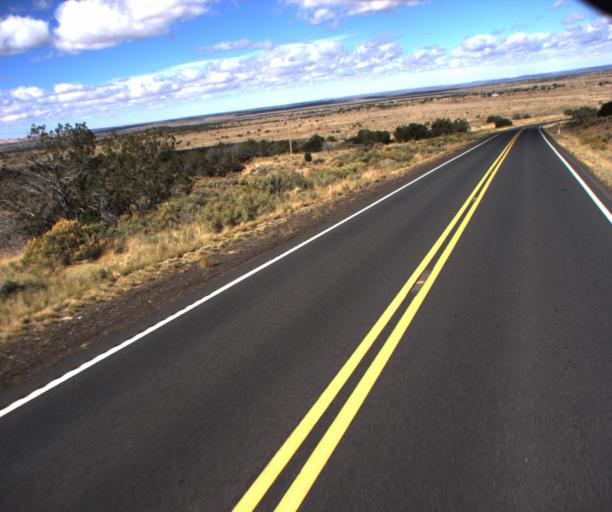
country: US
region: Arizona
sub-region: Apache County
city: Houck
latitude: 35.0350
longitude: -109.2627
